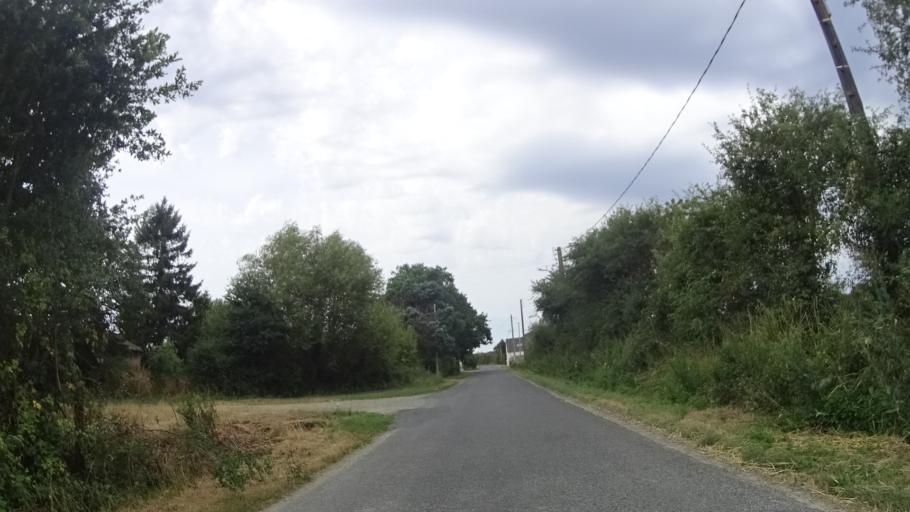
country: FR
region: Pays de la Loire
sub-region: Departement de la Loire-Atlantique
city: Fay-de-Bretagne
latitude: 47.4238
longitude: -1.7583
